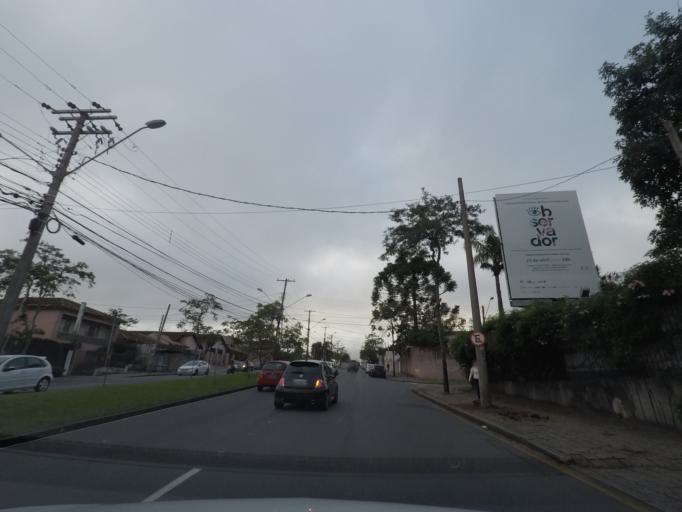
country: BR
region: Parana
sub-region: Curitiba
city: Curitiba
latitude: -25.4423
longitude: -49.2479
